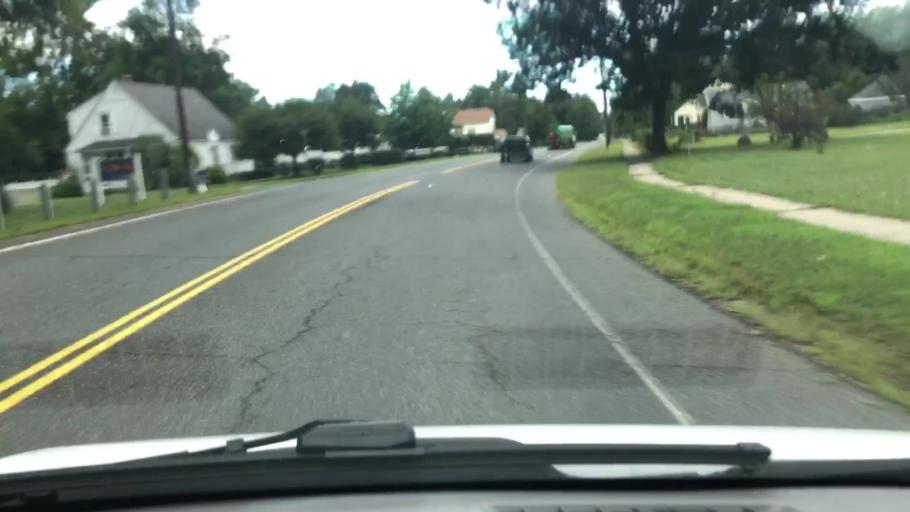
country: US
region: Massachusetts
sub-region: Franklin County
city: Turners Falls
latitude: 42.5942
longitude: -72.5468
